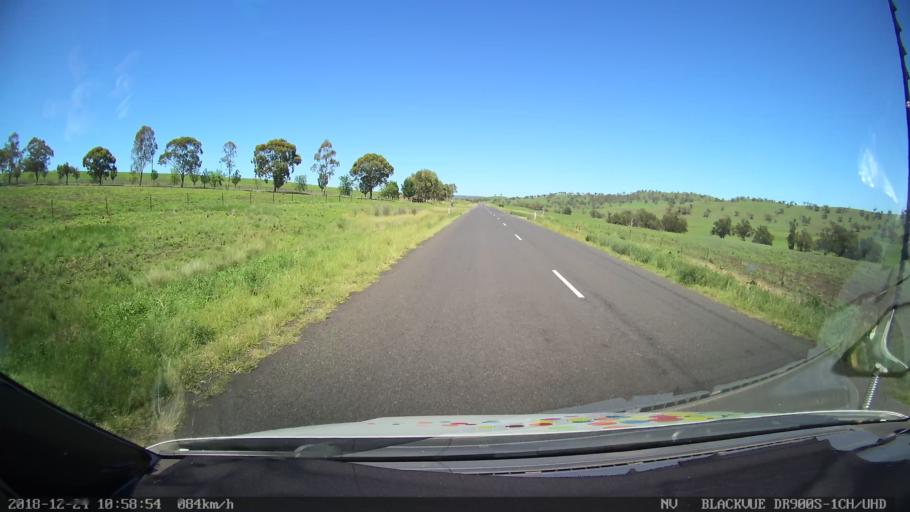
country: AU
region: New South Wales
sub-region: Upper Hunter Shire
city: Merriwa
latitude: -32.0525
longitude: 150.4039
